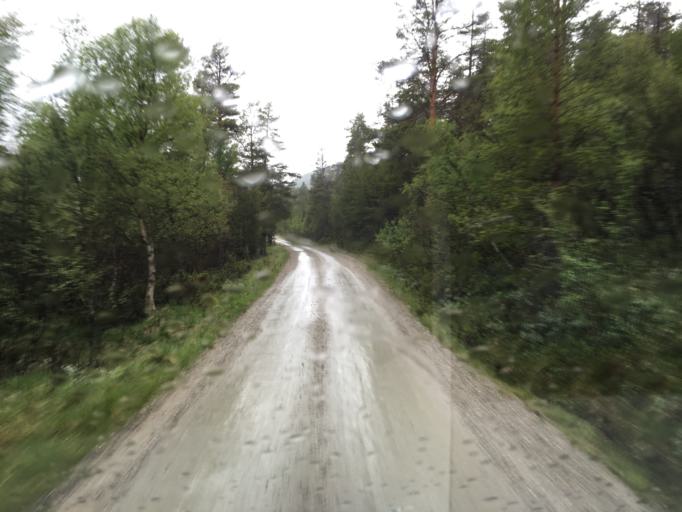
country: NO
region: Hedmark
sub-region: Folldal
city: Folldal
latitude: 62.0663
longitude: 9.9244
